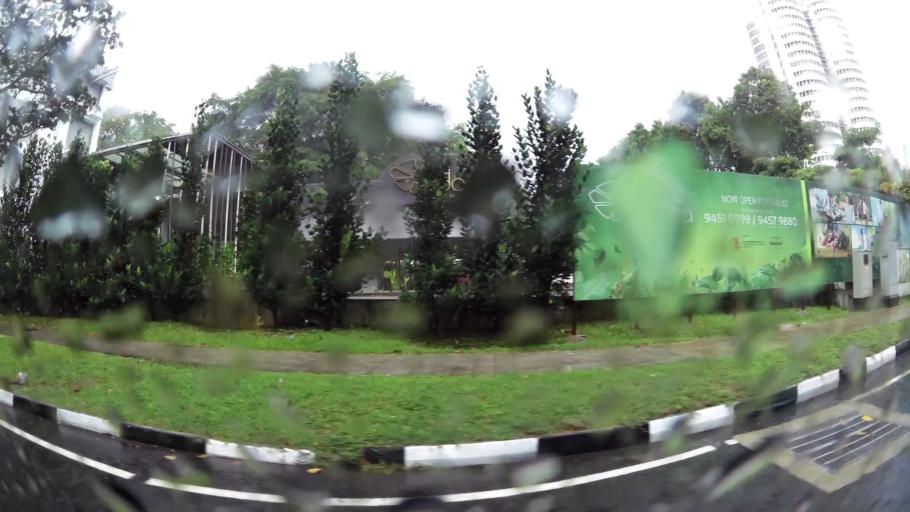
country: SG
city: Singapore
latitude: 1.3680
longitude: 103.8307
